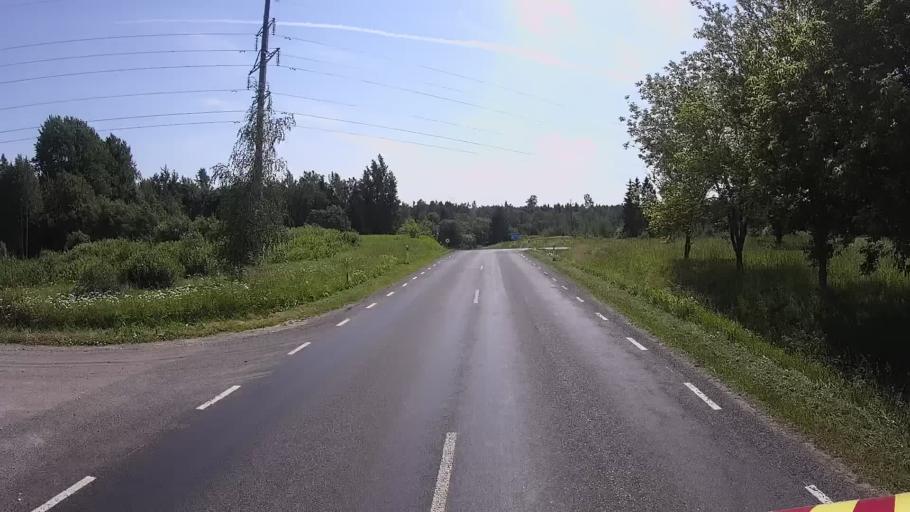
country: EE
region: Viljandimaa
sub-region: Karksi vald
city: Karksi-Nuia
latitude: 58.0924
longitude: 25.5590
